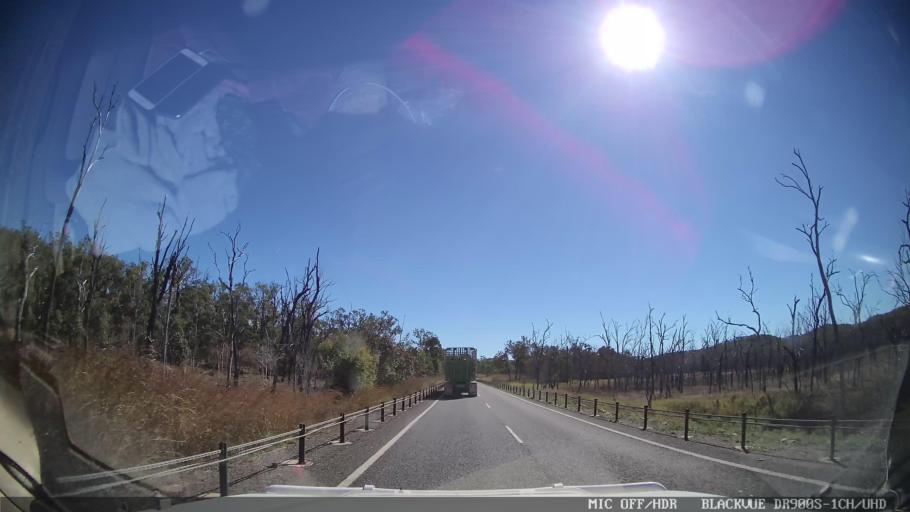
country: AU
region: Queensland
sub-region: Gladstone
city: Toolooa
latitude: -24.1574
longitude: 151.2141
